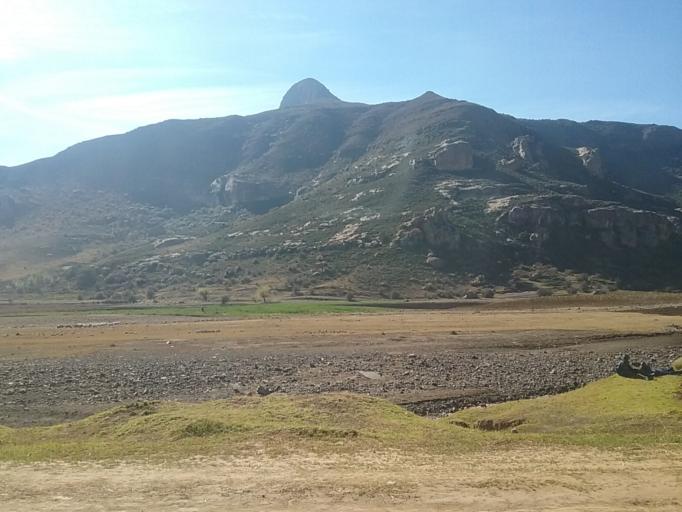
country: LS
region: Berea
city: Teyateyaneng
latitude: -29.2507
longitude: 27.9130
